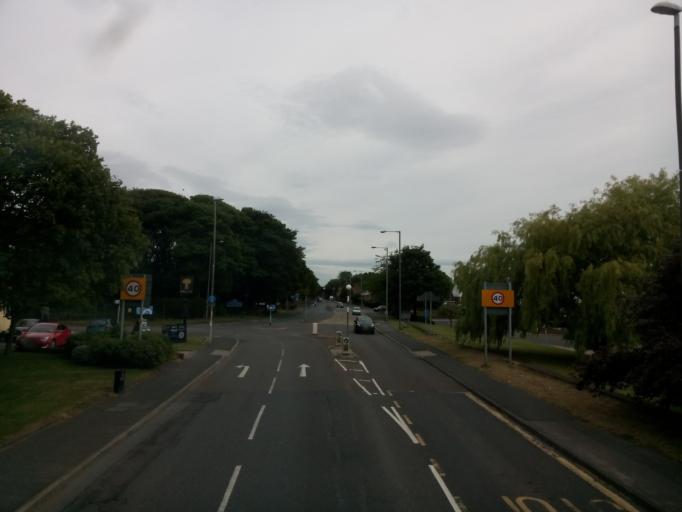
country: GB
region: England
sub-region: County Durham
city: Chester-le-Street
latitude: 54.8795
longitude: -1.5758
